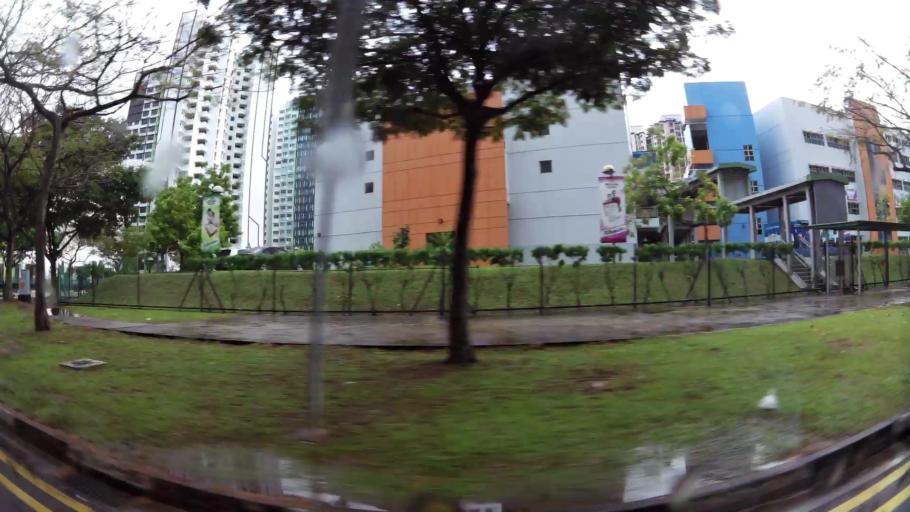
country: MY
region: Johor
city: Kampung Pasir Gudang Baru
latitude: 1.3917
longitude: 103.8787
